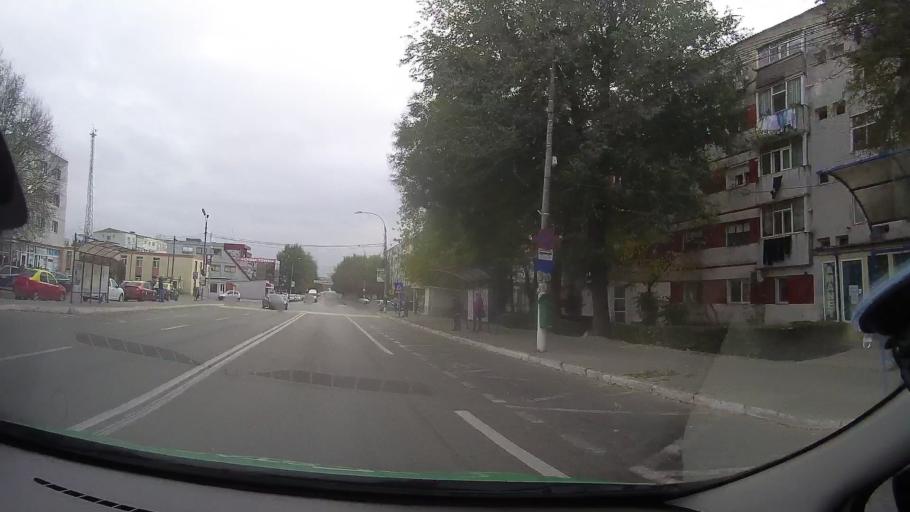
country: RO
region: Constanta
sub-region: Municipiul Medgidia
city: Medgidia
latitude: 44.2608
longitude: 28.2627
